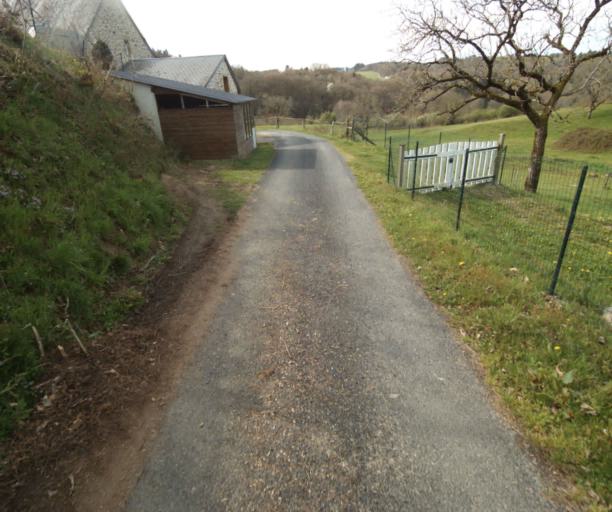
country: FR
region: Limousin
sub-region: Departement de la Correze
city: Correze
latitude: 45.3488
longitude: 1.8629
